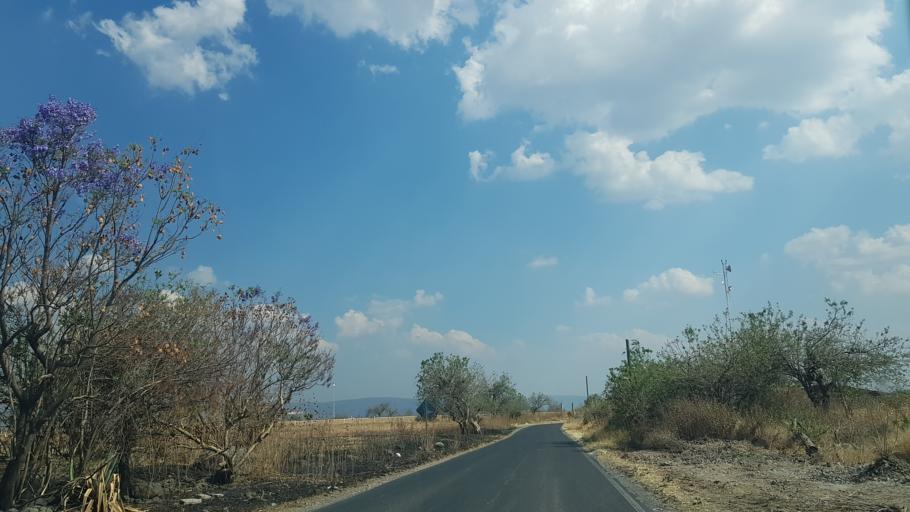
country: MX
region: Puebla
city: Atlixco
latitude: 18.9233
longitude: -98.4835
